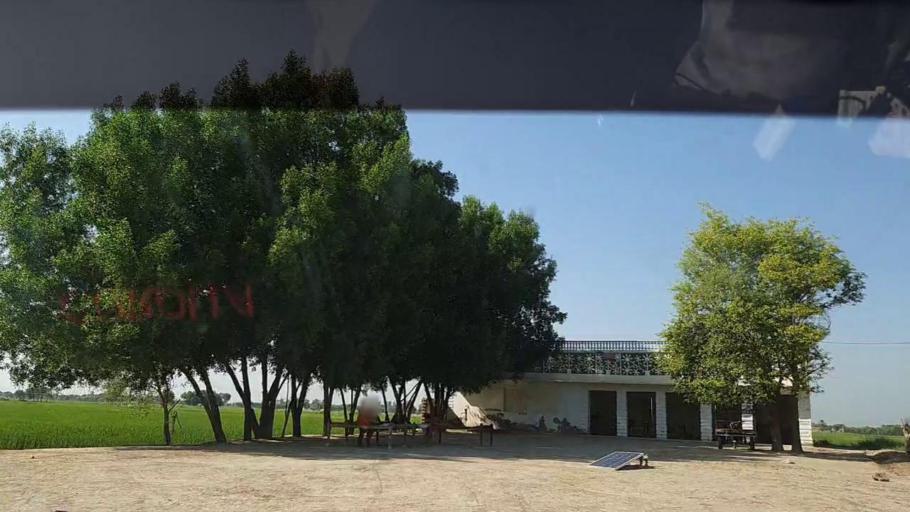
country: PK
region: Sindh
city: Ghauspur
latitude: 28.1807
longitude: 69.0265
